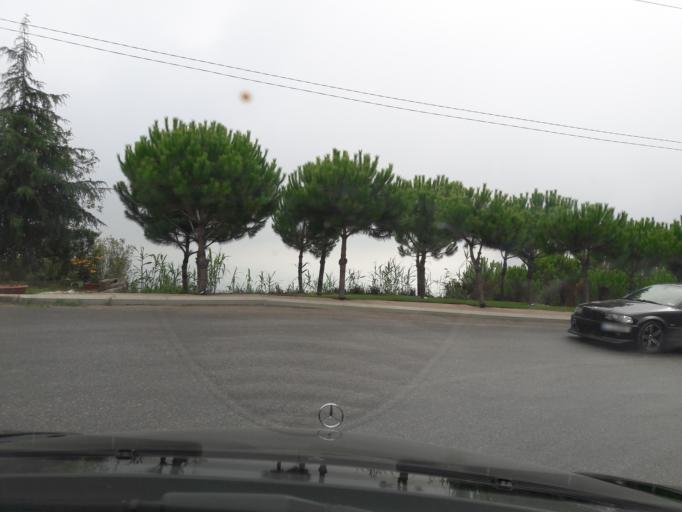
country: LB
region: Mont-Liban
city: Djounie
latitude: 33.9874
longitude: 35.6829
